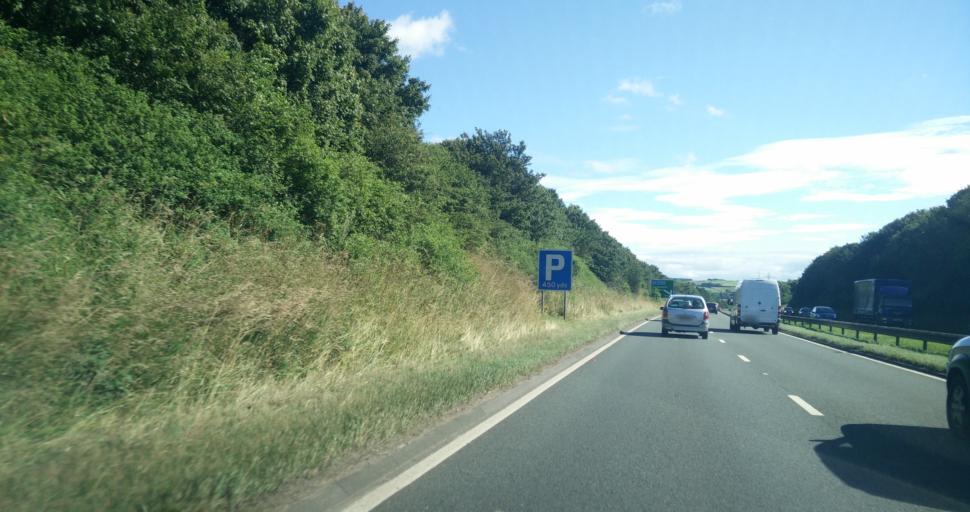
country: GB
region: England
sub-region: County Durham
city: Houghton-le-Spring
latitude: 54.8786
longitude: -1.4526
